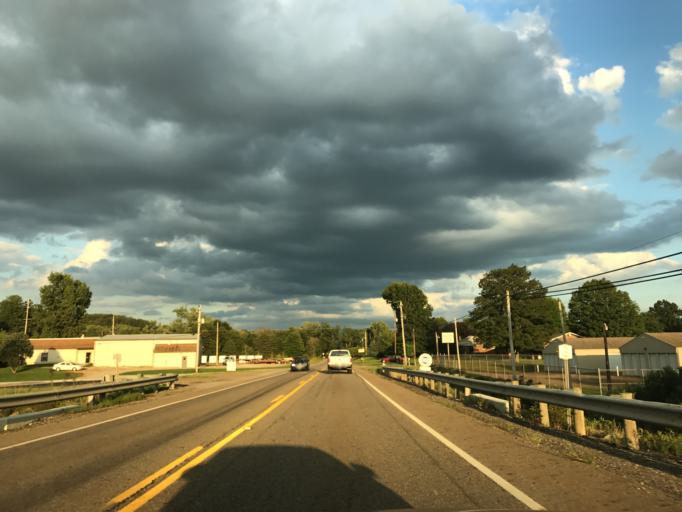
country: US
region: Ohio
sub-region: Stark County
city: East Canton
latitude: 40.7791
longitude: -81.2585
